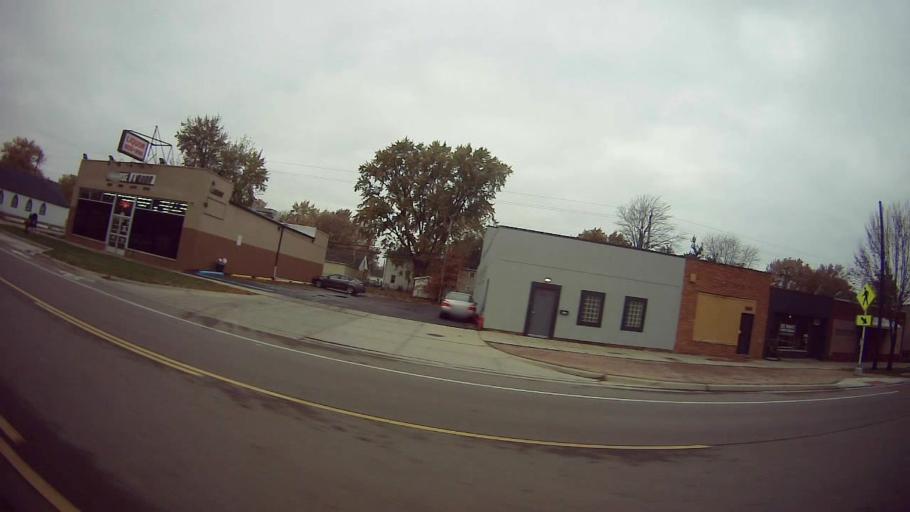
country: US
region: Michigan
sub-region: Oakland County
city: Ferndale
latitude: 42.4740
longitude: -83.1234
